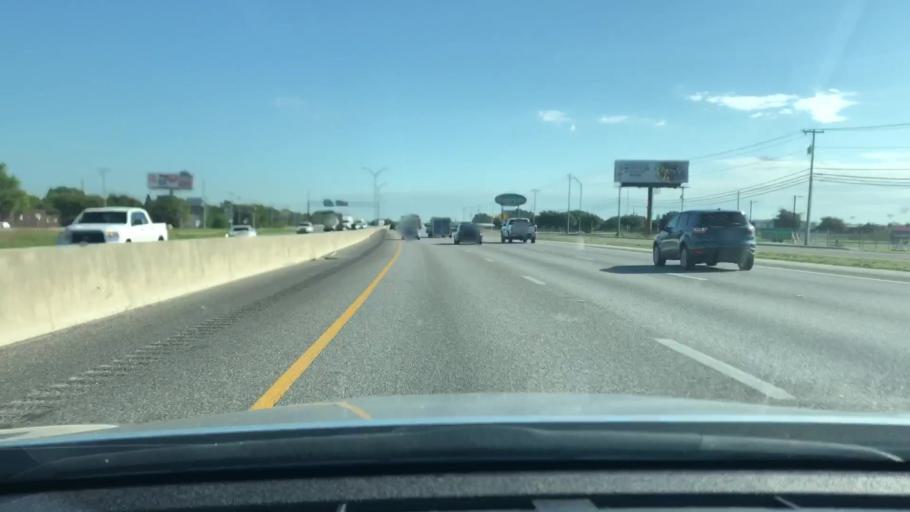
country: US
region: Texas
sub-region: Guadalupe County
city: Northcliff
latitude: 29.6547
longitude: -98.1871
